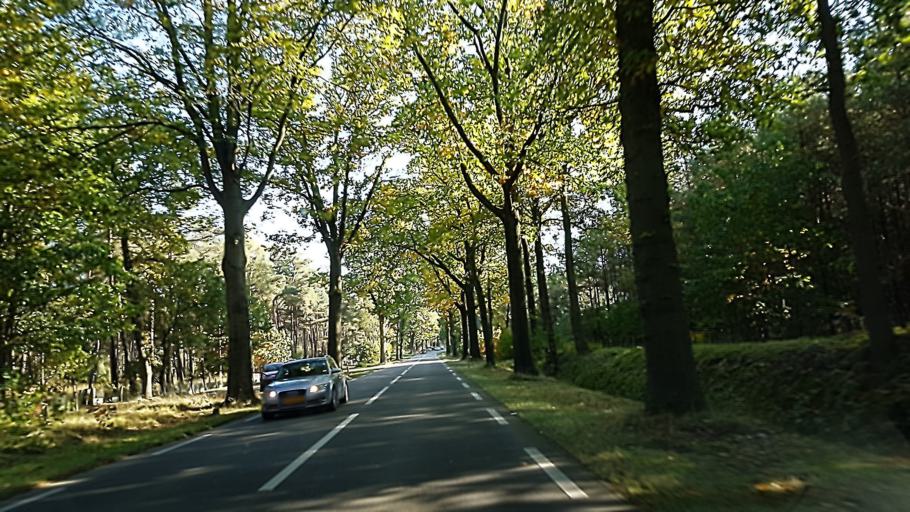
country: BE
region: Flanders
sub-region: Provincie Antwerpen
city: Stabroek
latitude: 51.3809
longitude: 4.3763
